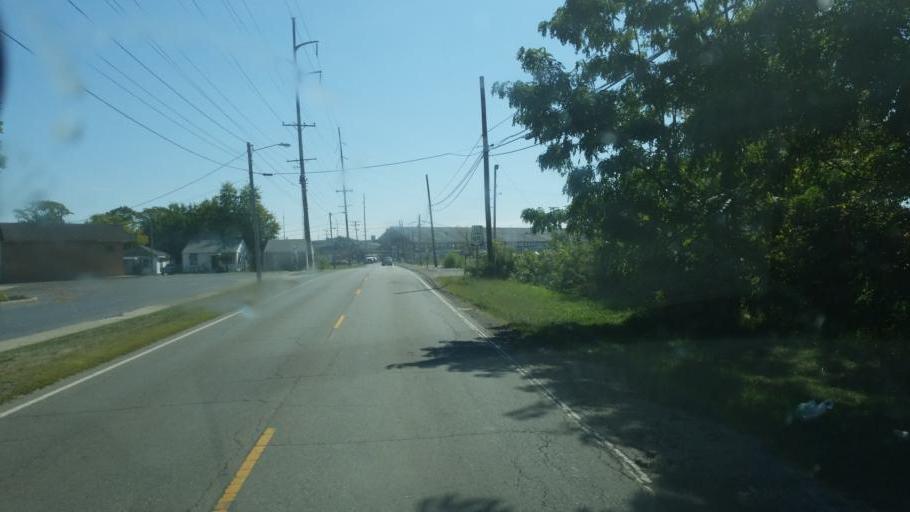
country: US
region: Ohio
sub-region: Marion County
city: Marion
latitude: 40.5909
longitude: -83.1473
